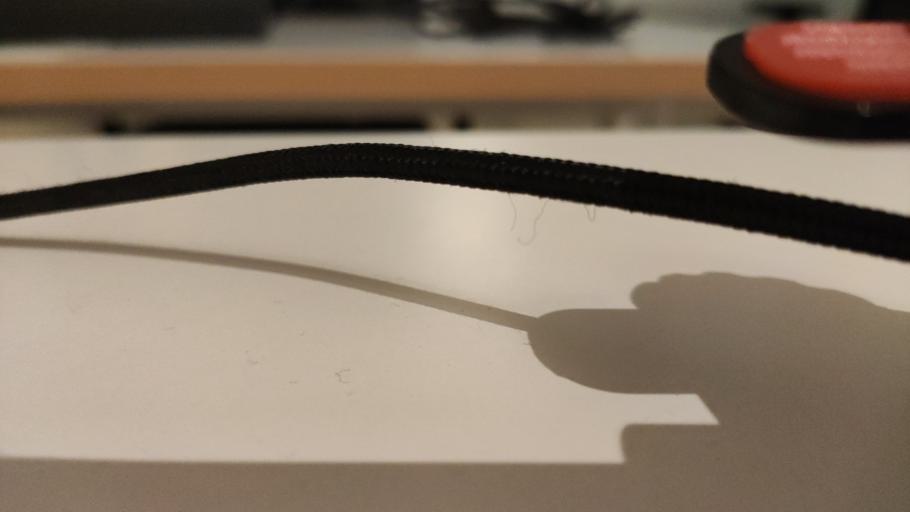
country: RU
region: Moskovskaya
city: Shaburnovo
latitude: 56.4278
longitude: 37.9520
